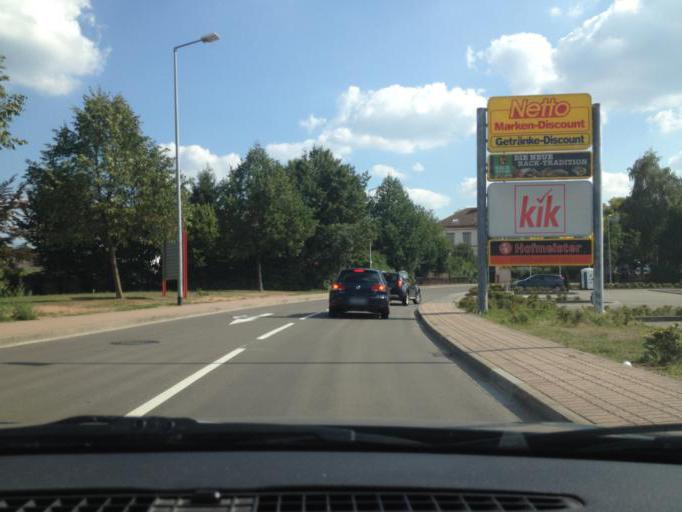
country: DE
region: Rheinland-Pfalz
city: Ramstein-Miesenbach
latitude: 49.4471
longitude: 7.5580
